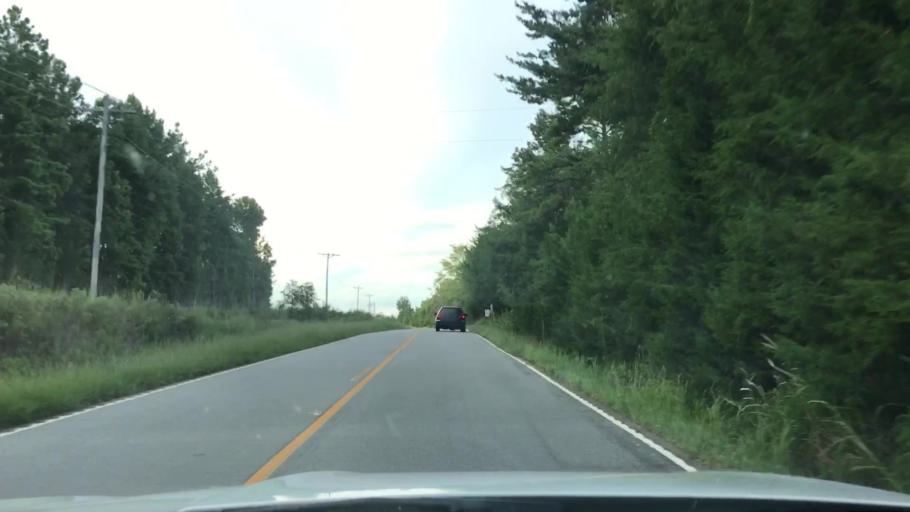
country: US
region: South Carolina
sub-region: Spartanburg County
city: Woodruff
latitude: 34.7634
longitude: -81.9152
